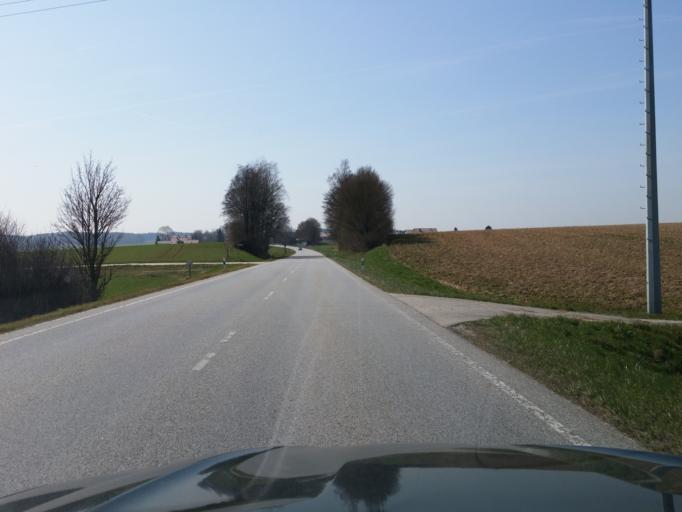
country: DE
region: Bavaria
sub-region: Lower Bavaria
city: Altfraunhofen
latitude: 48.4628
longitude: 12.1508
